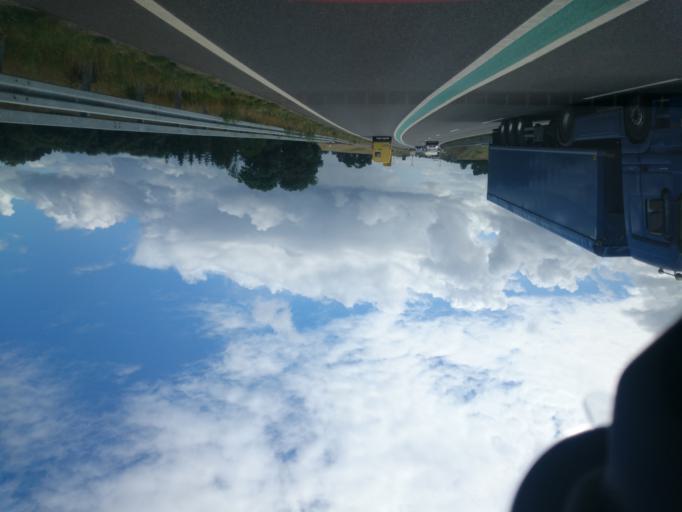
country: DE
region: Mecklenburg-Vorpommern
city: Samtens
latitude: 54.3555
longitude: 13.3053
